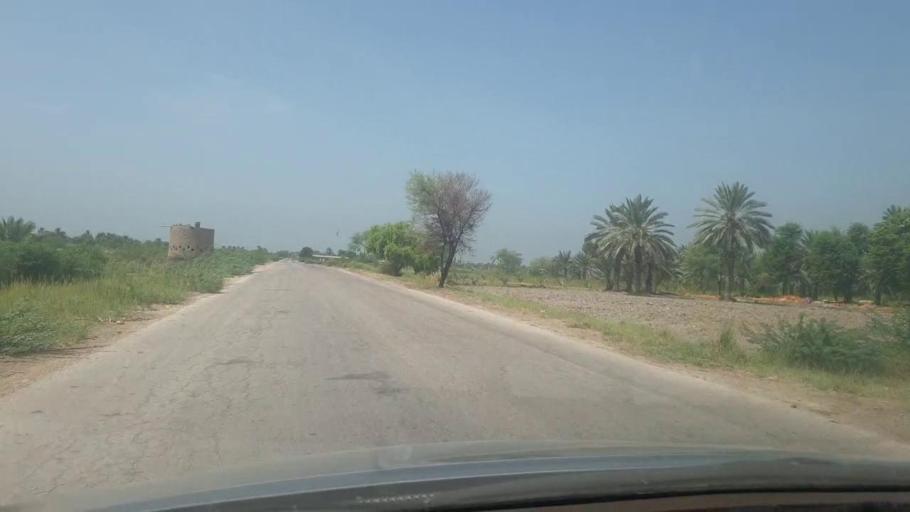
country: PK
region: Sindh
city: Ranipur
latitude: 27.2540
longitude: 68.5855
